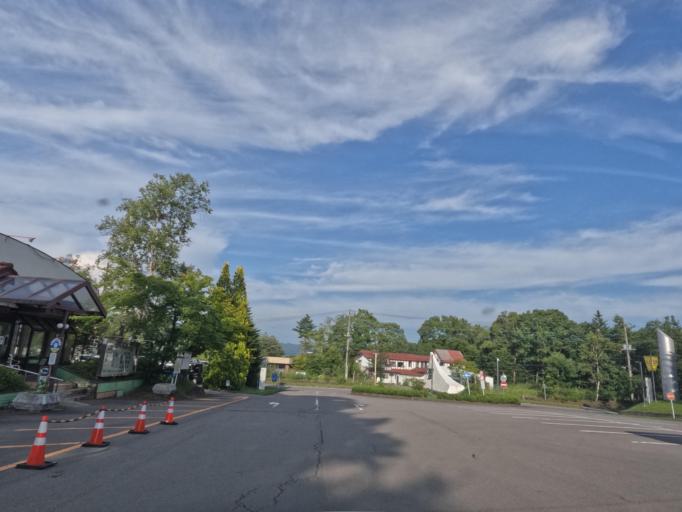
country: JP
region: Nagano
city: Komoro
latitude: 36.4747
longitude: 138.5485
